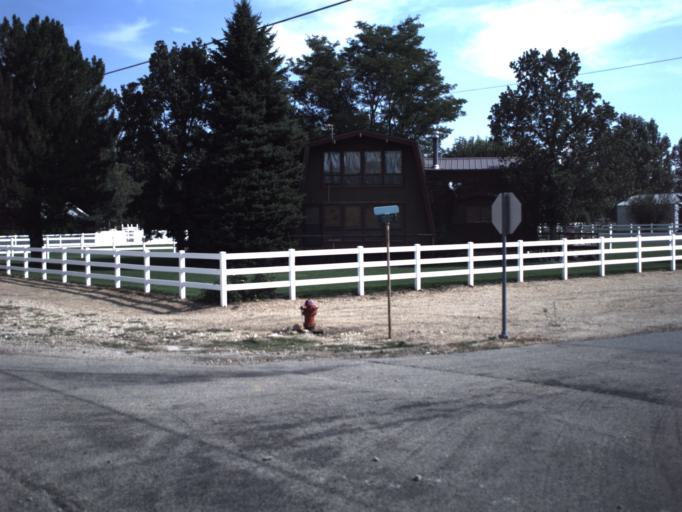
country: US
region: Utah
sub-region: Wasatch County
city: Midway
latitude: 40.4662
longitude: -111.4717
